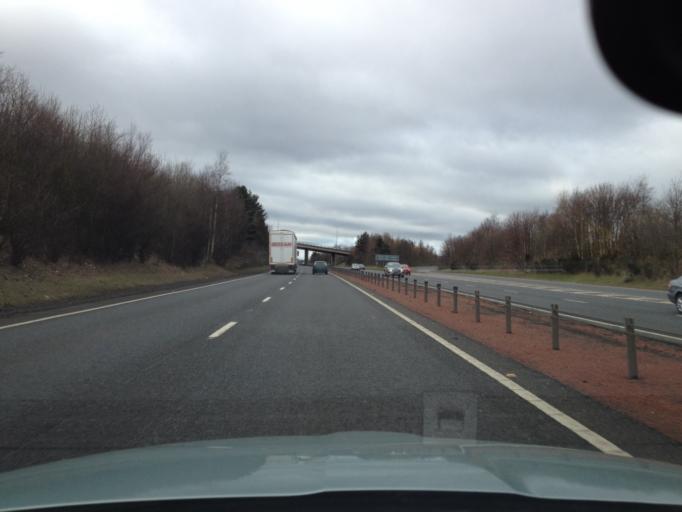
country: GB
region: Scotland
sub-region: East Lothian
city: Prestonpans
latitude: 55.9463
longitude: -2.9819
